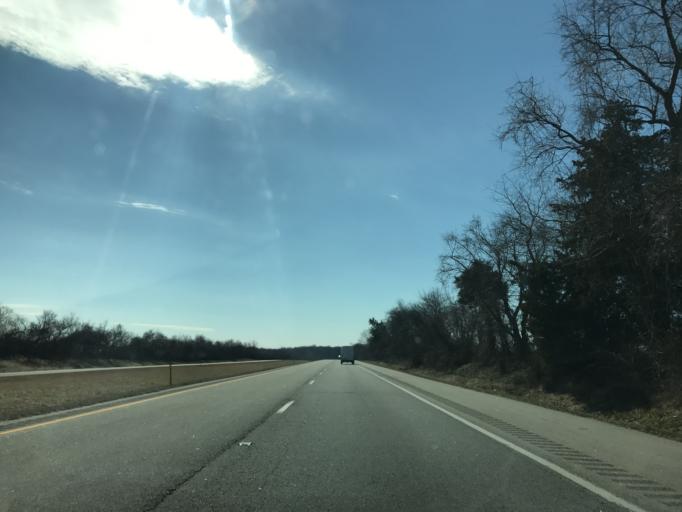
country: US
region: Maryland
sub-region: Queen Anne's County
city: Kingstown
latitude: 39.1149
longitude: -75.9483
